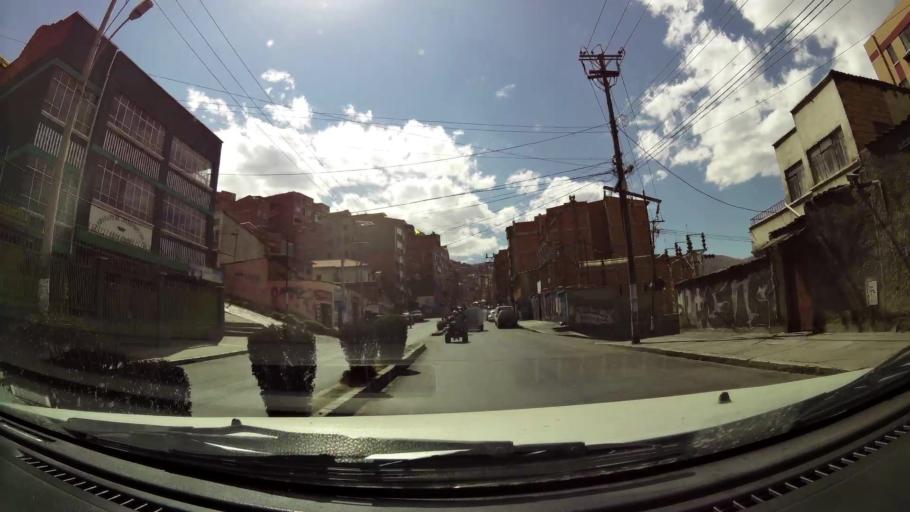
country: BO
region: La Paz
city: La Paz
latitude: -16.4916
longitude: -68.1252
